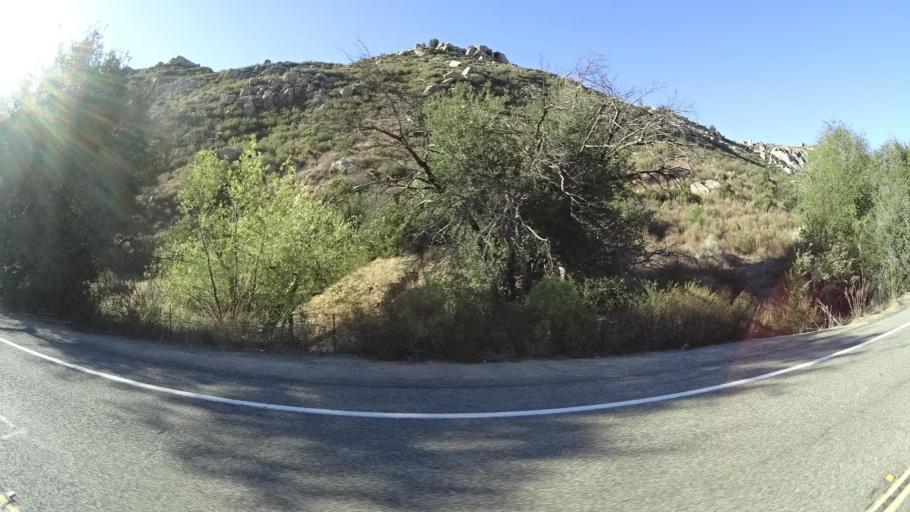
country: MX
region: Baja California
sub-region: Tecate
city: Hacienda Tecate
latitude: 32.5959
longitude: -116.5419
